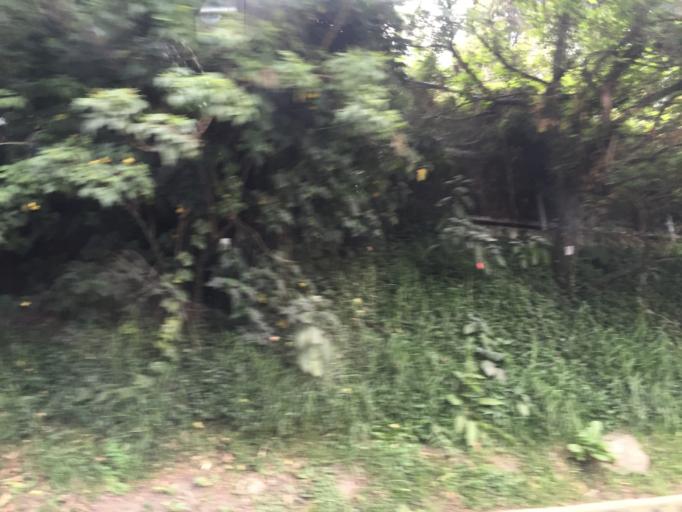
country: CO
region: Bogota D.C.
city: Bogota
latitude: 4.6009
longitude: -74.0635
